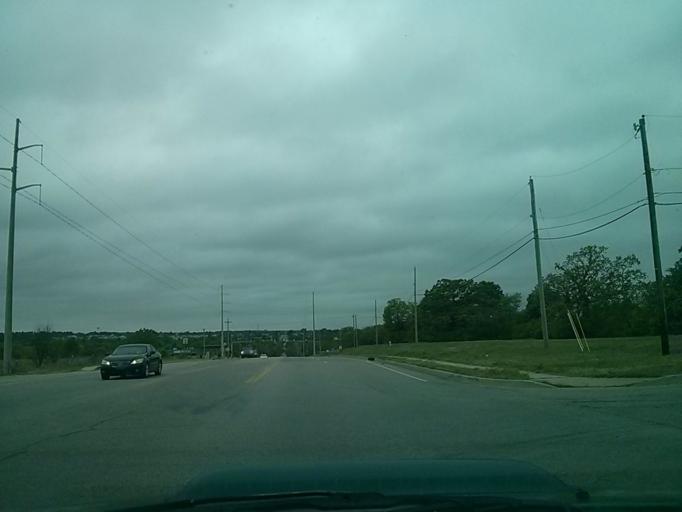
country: US
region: Oklahoma
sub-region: Tulsa County
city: Oakhurst
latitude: 36.0754
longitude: -96.0088
